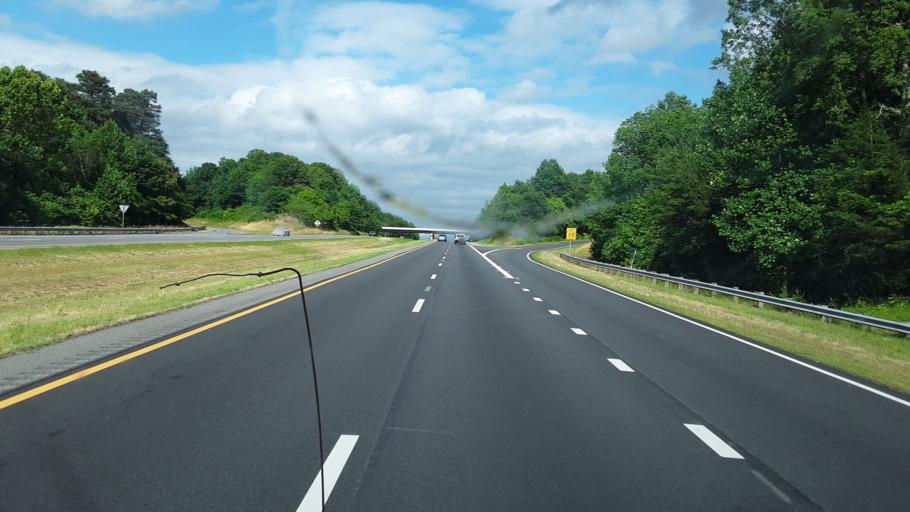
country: US
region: Virginia
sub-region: City of Danville
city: Danville
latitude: 36.5463
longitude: -79.4053
